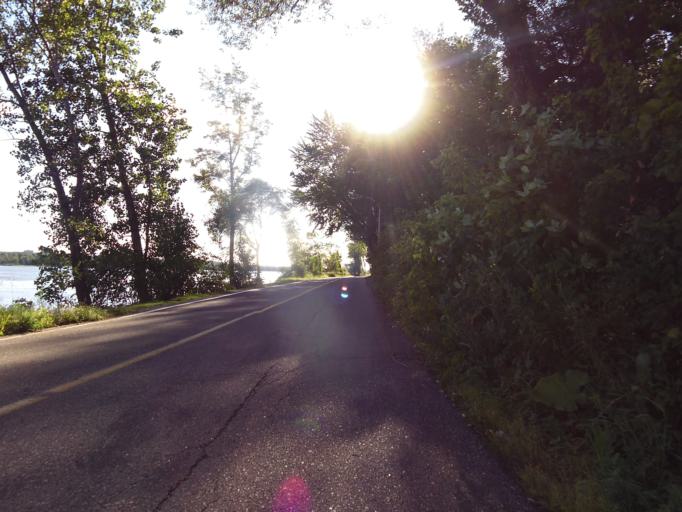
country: CA
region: Quebec
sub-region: Outaouais
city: Gatineau
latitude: 45.4777
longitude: -75.5905
